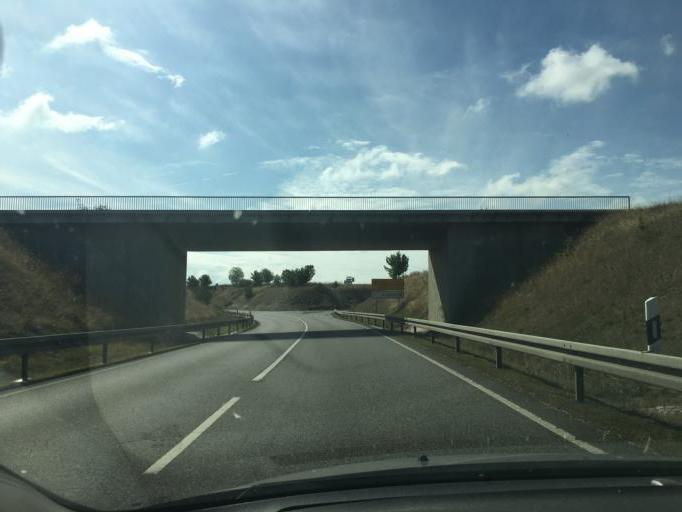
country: DE
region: Thuringia
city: Mittelpollnitz
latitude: 50.7505
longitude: 11.9069
